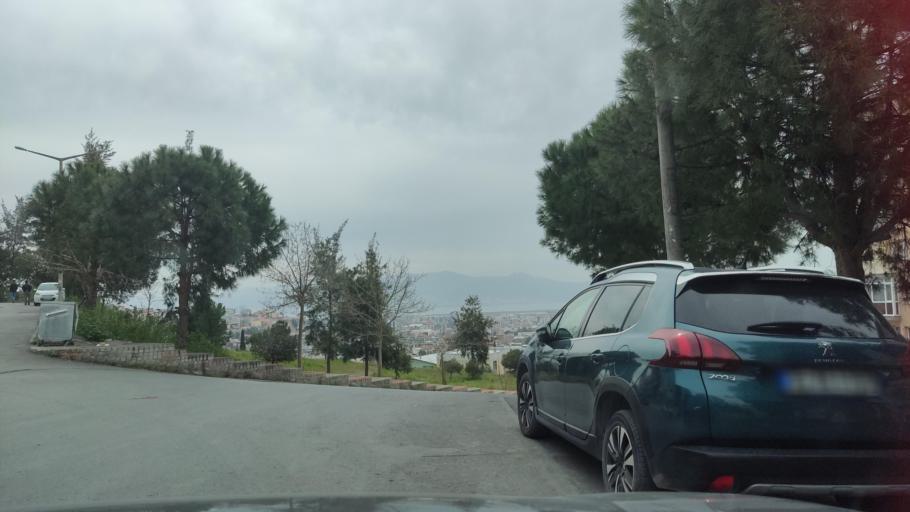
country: TR
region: Izmir
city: Karsiyaka
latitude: 38.5043
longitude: 27.0700
